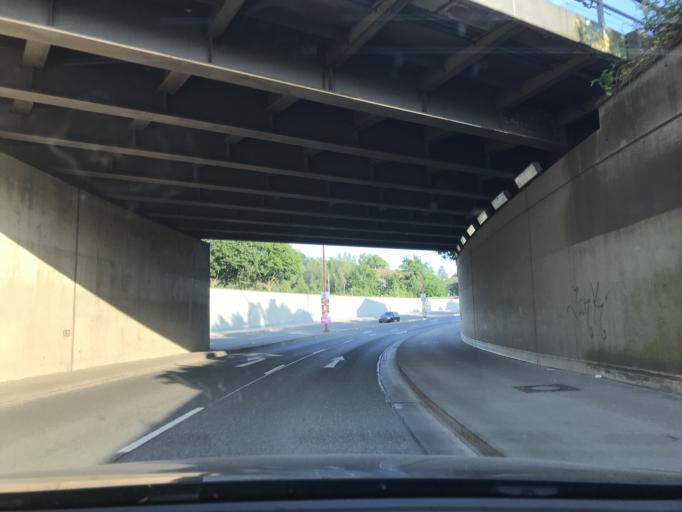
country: DE
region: Lower Saxony
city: Lehrte
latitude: 52.3856
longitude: 9.9731
